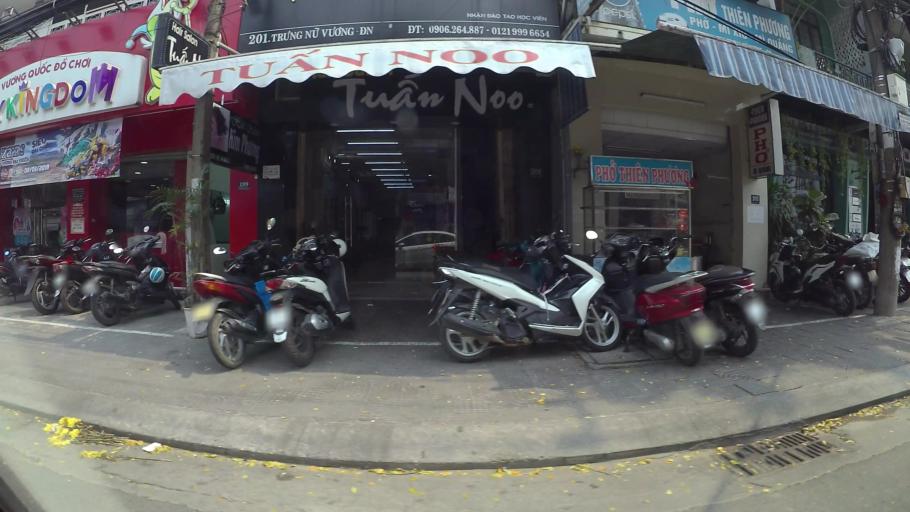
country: VN
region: Da Nang
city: Da Nang
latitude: 16.0535
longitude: 108.2192
